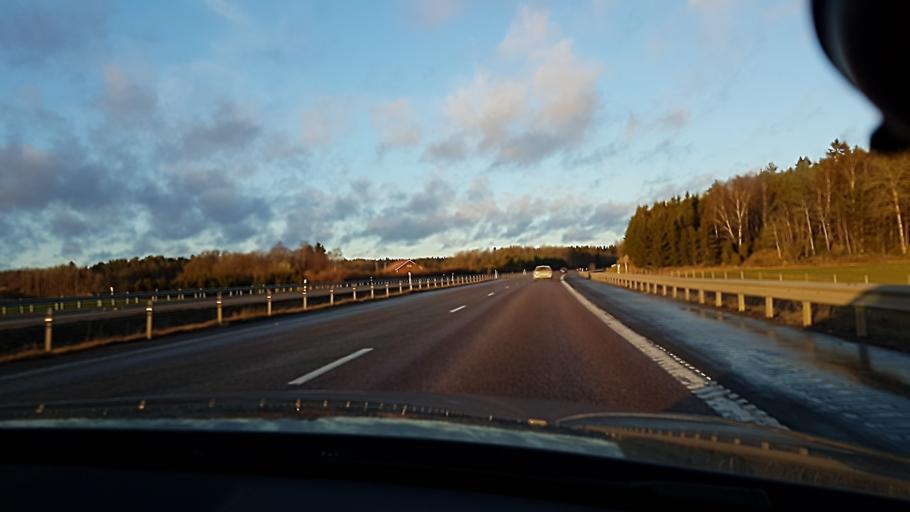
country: SE
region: Soedermanland
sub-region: Trosa Kommun
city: Vagnharad
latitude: 59.0446
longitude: 17.5651
